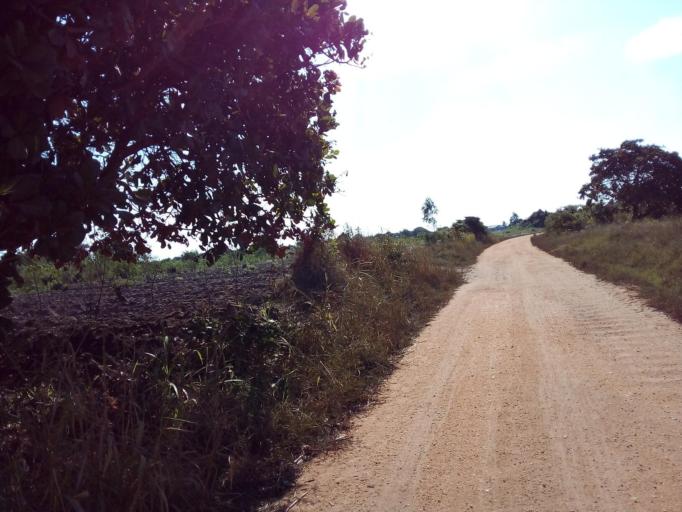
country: MZ
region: Zambezia
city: Quelimane
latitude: -17.5692
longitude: 36.6384
